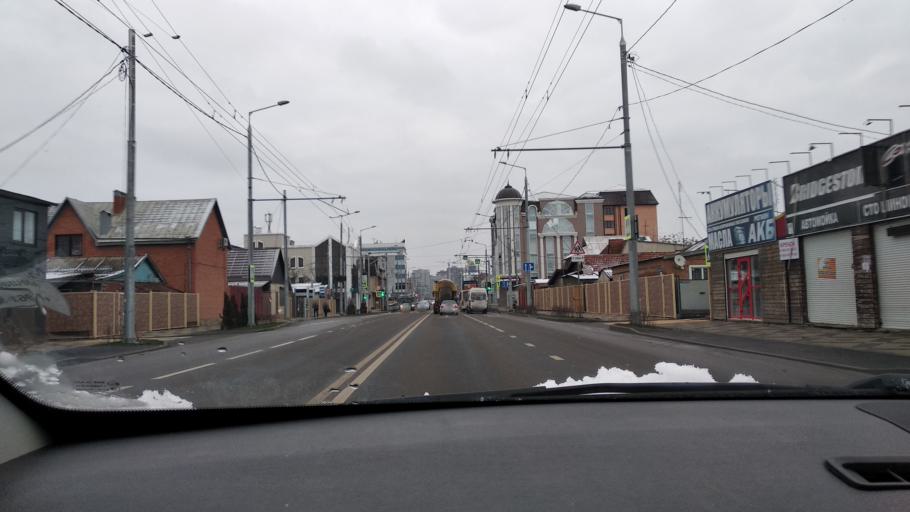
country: RU
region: Krasnodarskiy
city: Krasnodar
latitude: 45.0467
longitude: 38.9578
